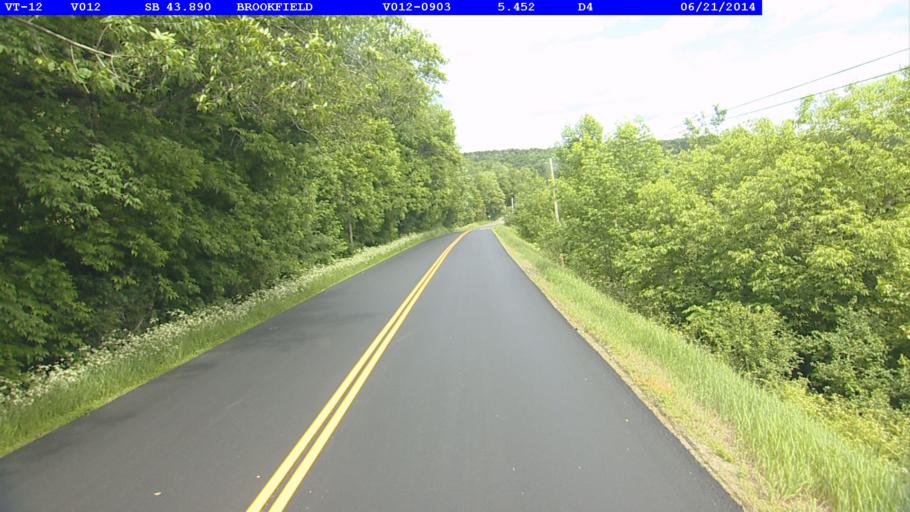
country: US
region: Vermont
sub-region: Washington County
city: Northfield
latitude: 44.0760
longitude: -72.6414
